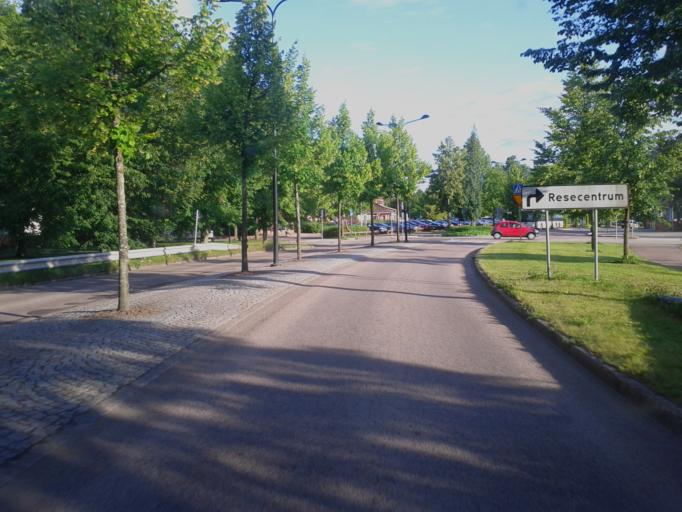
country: SE
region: Dalarna
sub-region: Borlange Kommun
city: Borlaenge
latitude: 60.4834
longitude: 15.4279
